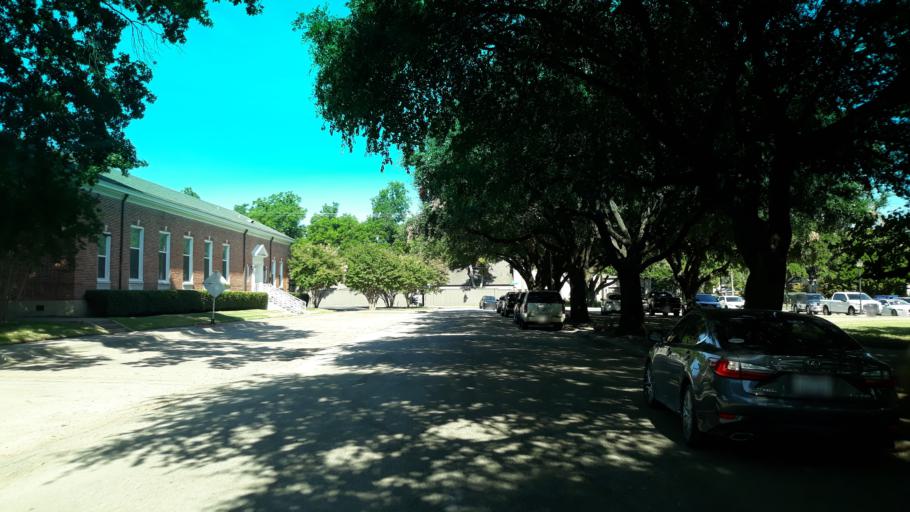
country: US
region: Texas
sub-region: Dallas County
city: Highland Park
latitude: 32.8248
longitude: -96.7613
